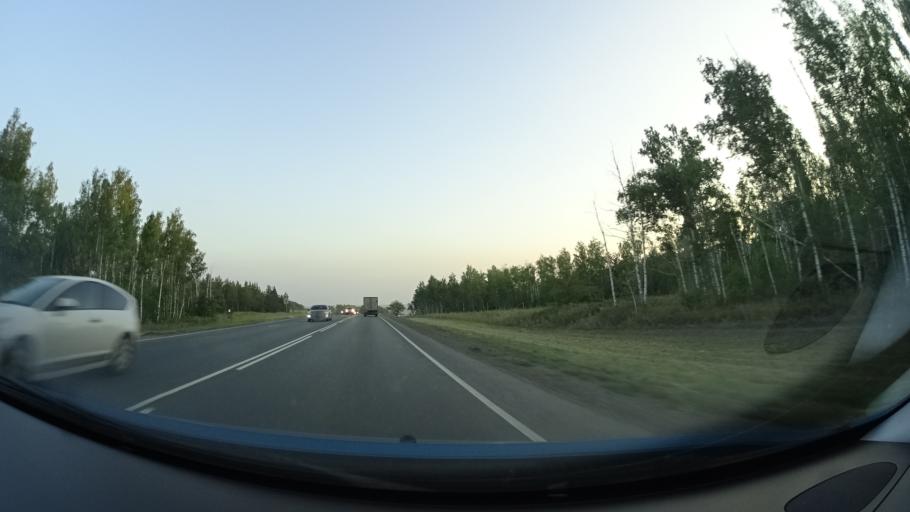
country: RU
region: Samara
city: Sernovodsk
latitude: 53.9164
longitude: 51.3043
